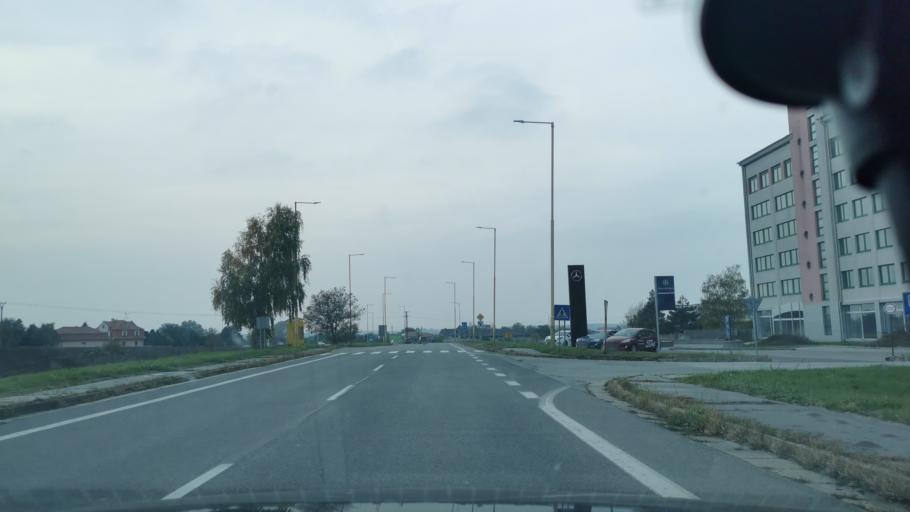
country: SK
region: Trnavsky
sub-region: Okres Skalica
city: Holic
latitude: 48.8002
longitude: 17.1550
